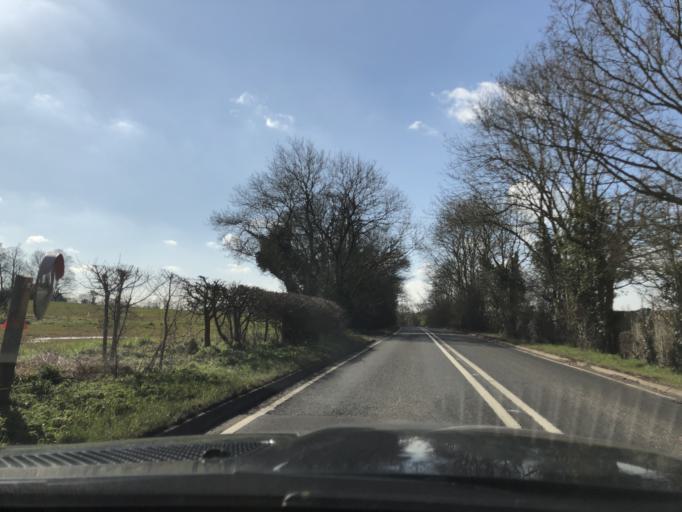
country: GB
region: England
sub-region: Warwickshire
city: Ryton on Dunsmore
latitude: 52.3219
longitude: -1.4211
